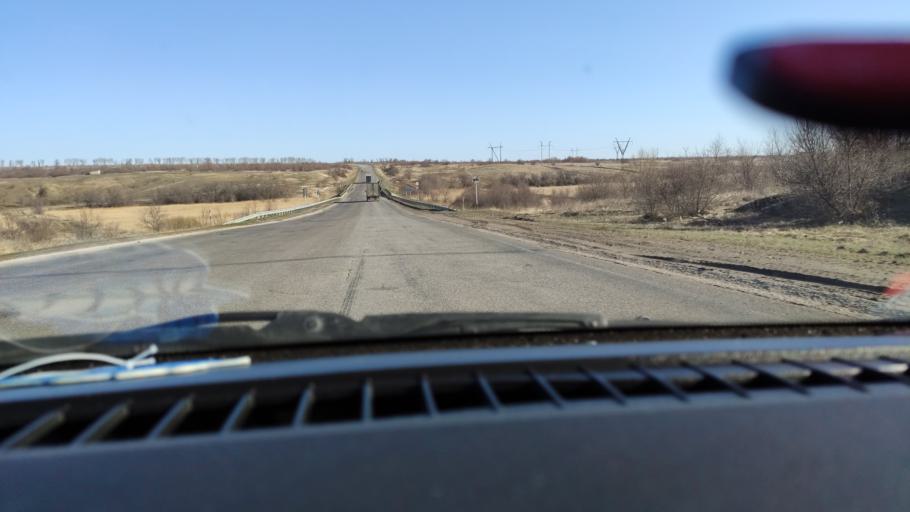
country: RU
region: Samara
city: Varlamovo
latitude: 53.0951
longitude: 48.3560
